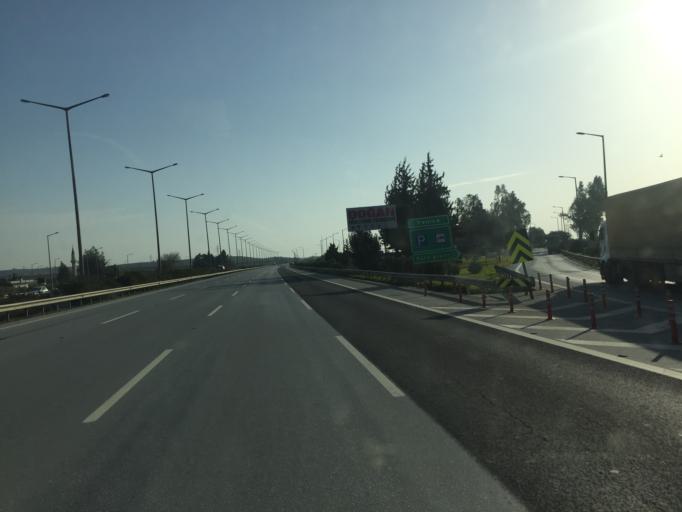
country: TR
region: Mersin
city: Yenice
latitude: 37.0235
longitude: 35.0602
